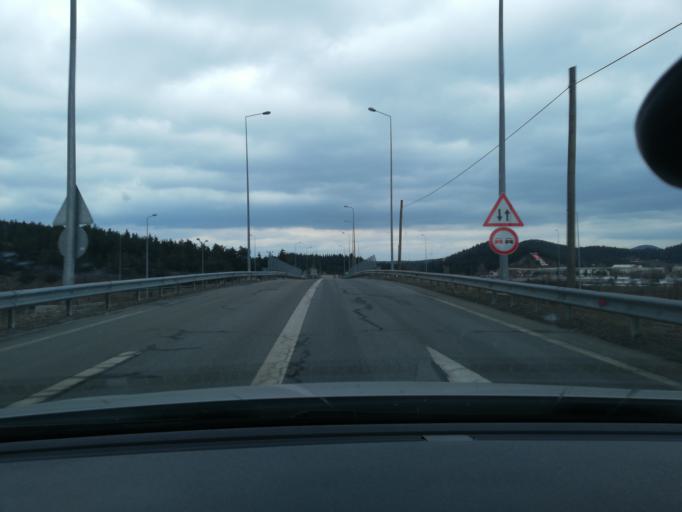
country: TR
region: Bolu
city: Gerede
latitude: 40.6114
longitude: 32.2527
